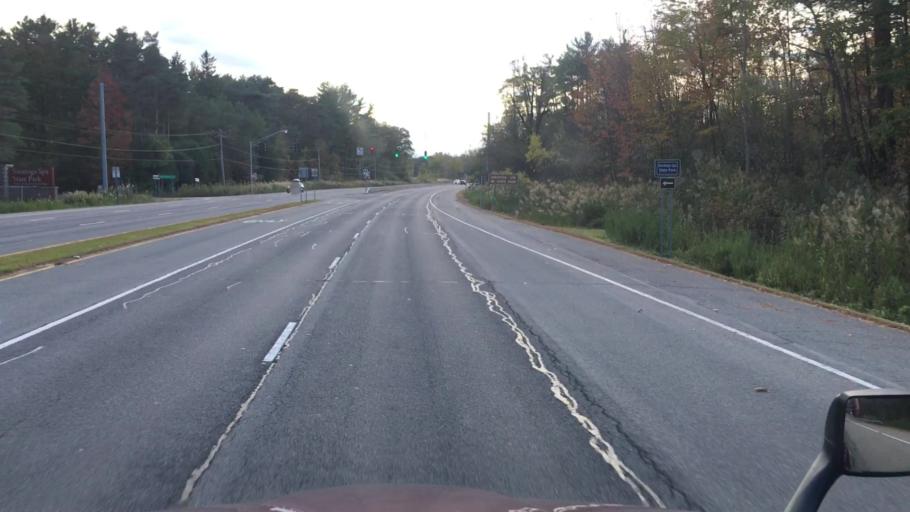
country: US
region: New York
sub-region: Saratoga County
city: Milton
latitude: 43.0496
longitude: -73.8124
